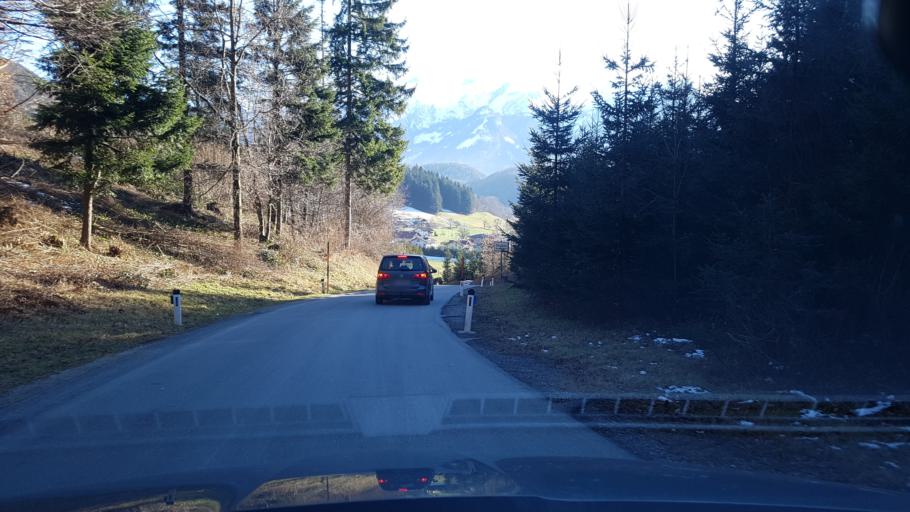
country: AT
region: Salzburg
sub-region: Politischer Bezirk Hallein
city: Golling an der Salzach
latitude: 47.6199
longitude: 13.1726
